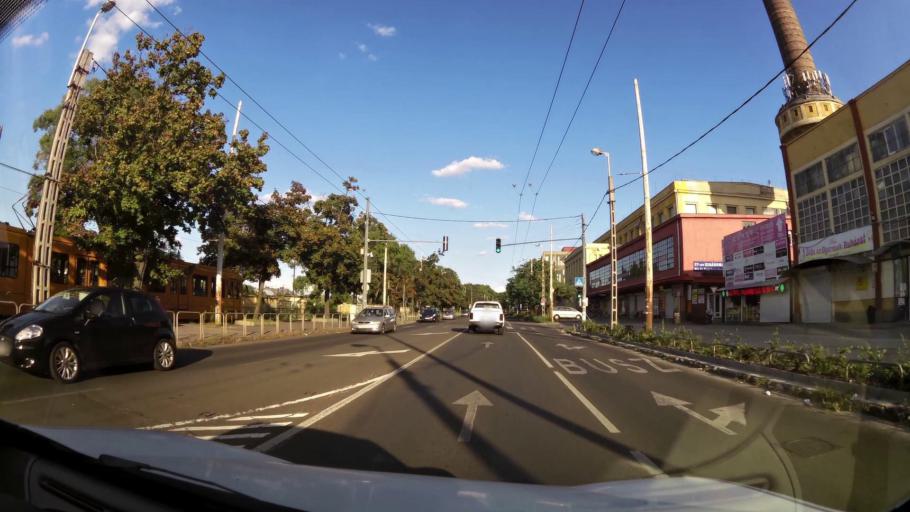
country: HU
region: Budapest
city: Budapest VIII. keruelet
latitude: 47.4884
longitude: 19.0989
